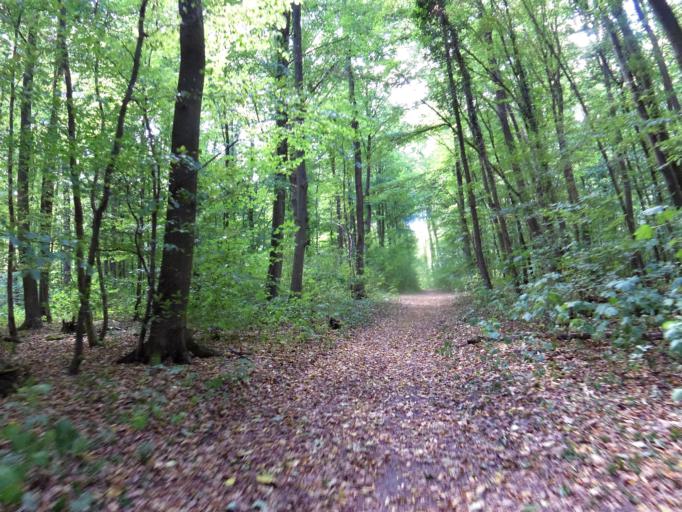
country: DE
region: Bavaria
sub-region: Regierungsbezirk Unterfranken
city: Hochberg
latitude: 49.7945
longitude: 9.8789
